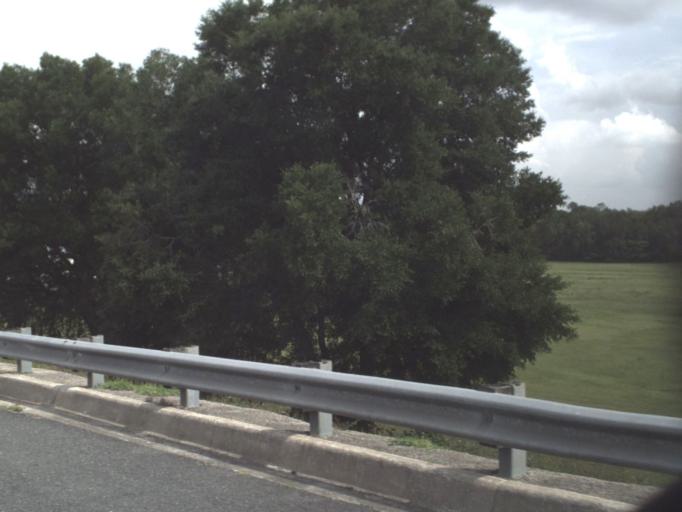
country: US
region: Florida
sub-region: Marion County
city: Belleview
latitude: 29.0551
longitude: -82.0431
